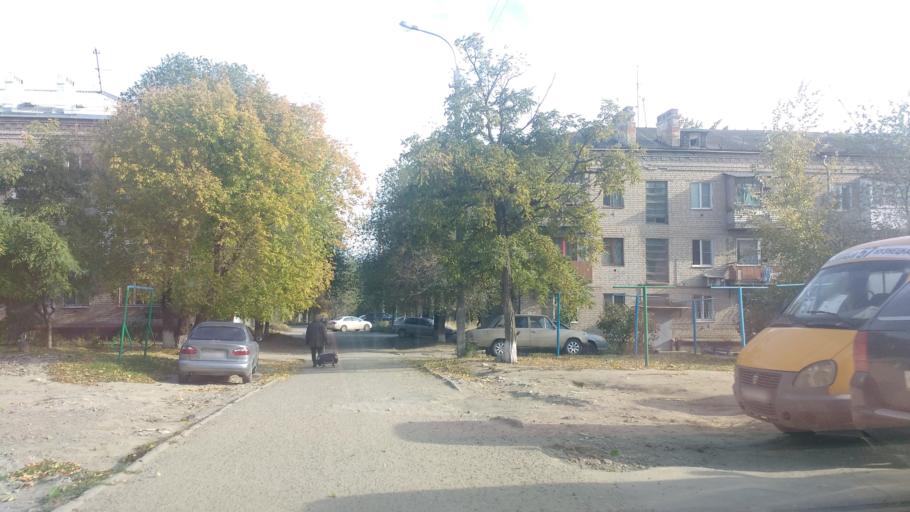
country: RU
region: Volgograd
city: Krasnoslobodsk
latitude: 48.7642
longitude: 44.5532
